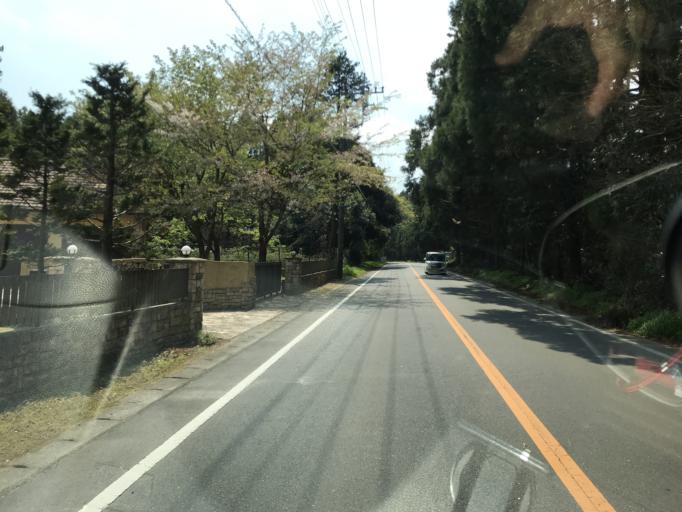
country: JP
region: Chiba
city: Omigawa
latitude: 35.8744
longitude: 140.5693
